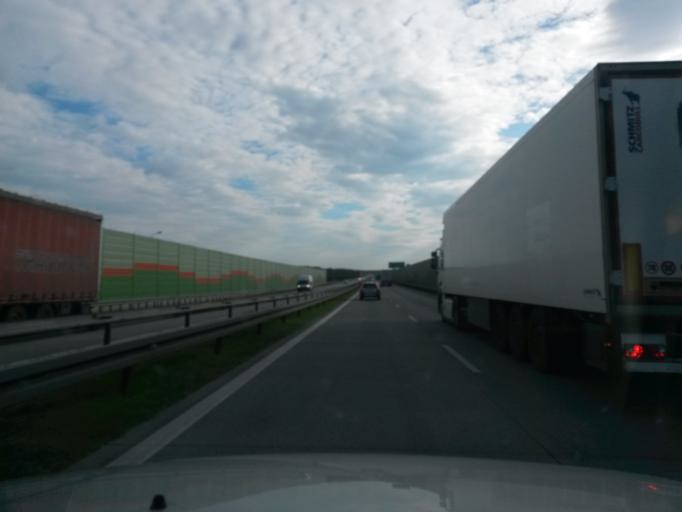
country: PL
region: Lodz Voivodeship
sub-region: Powiat tomaszowski
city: Tomaszow Mazowiecki
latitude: 51.5375
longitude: 19.9596
